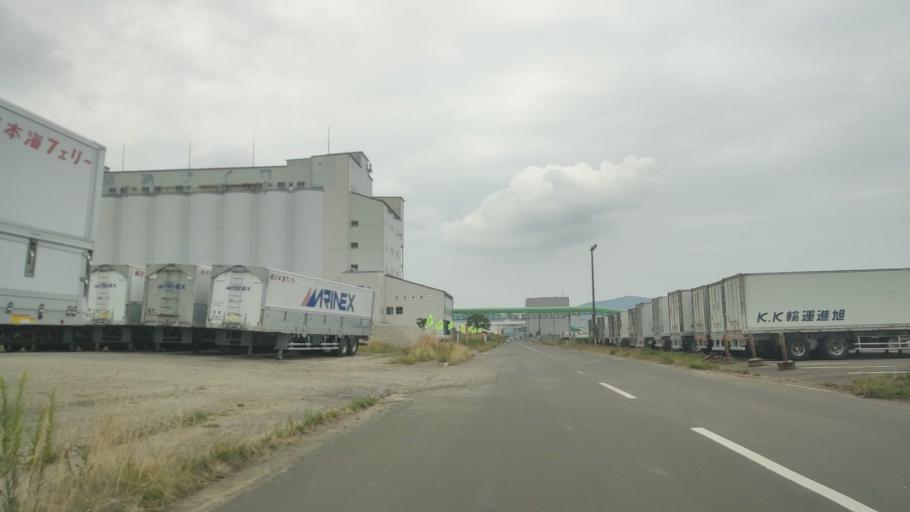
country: JP
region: Hokkaido
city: Otaru
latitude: 43.1878
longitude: 141.0235
